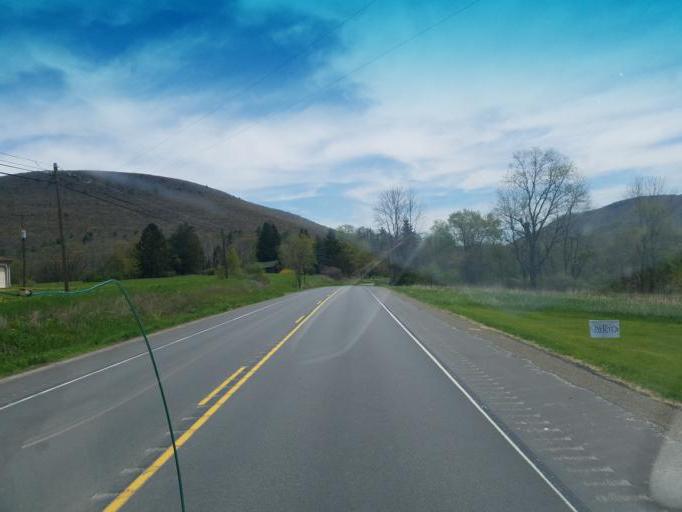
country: US
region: Pennsylvania
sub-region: Potter County
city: Galeton
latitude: 41.7452
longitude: -77.6013
